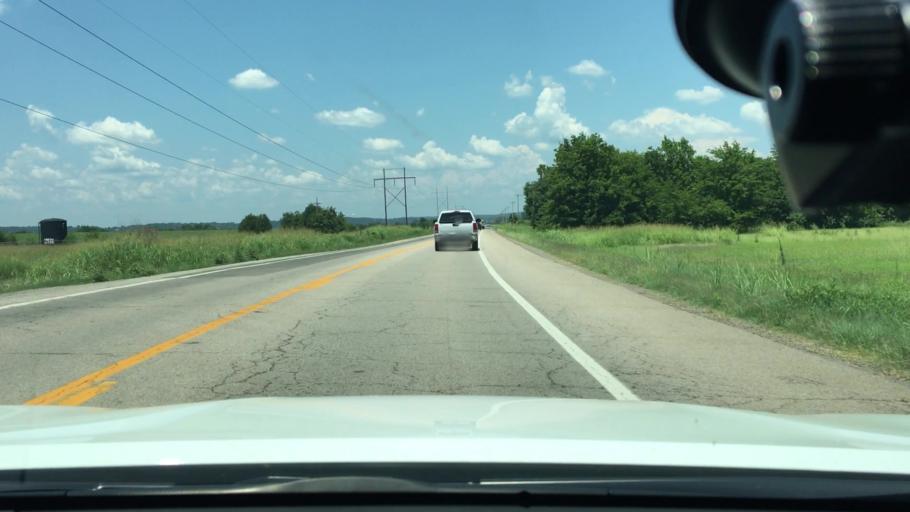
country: US
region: Arkansas
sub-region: Crawford County
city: Van Buren
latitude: 35.3928
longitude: -94.3304
